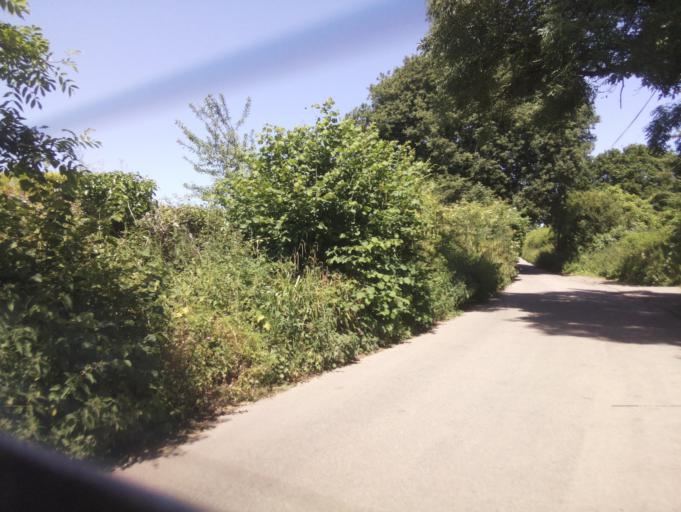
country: GB
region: England
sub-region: Devon
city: Dartmouth
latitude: 50.3909
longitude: -3.5677
